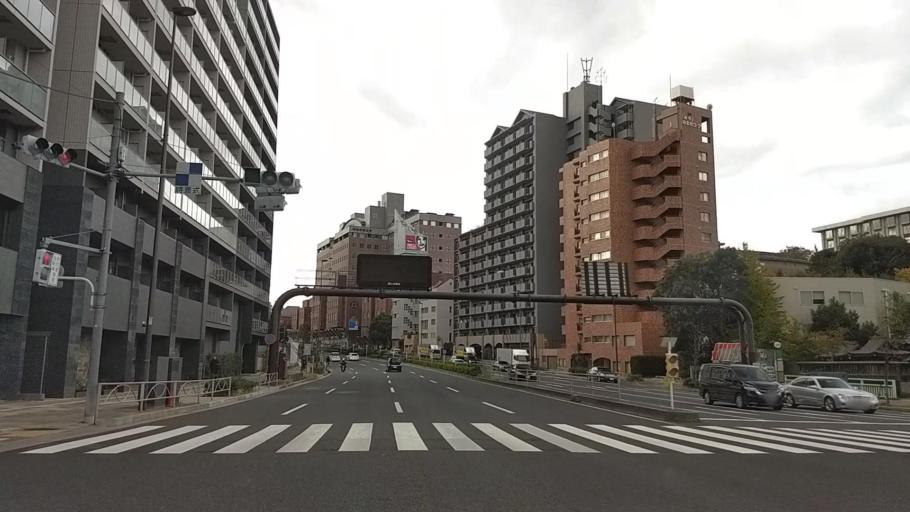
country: JP
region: Tokyo
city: Tokyo
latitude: 35.6399
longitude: 139.7326
